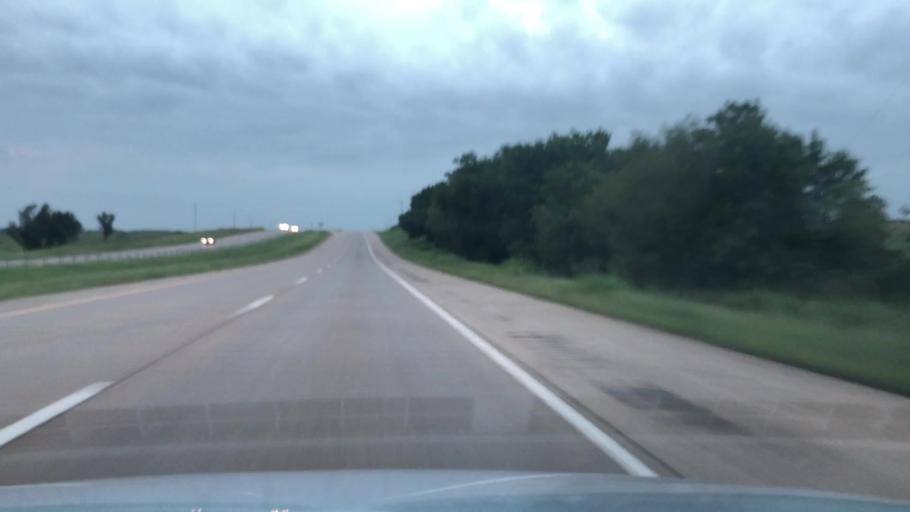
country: US
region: Oklahoma
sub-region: Washington County
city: Bartlesville
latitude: 36.6238
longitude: -95.9353
